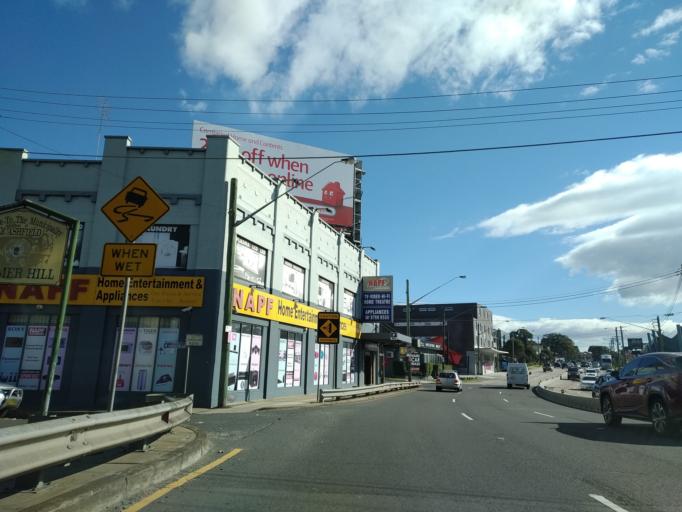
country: AU
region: New South Wales
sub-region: Ashfield
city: Summer Hill
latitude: -33.8897
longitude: 151.1448
